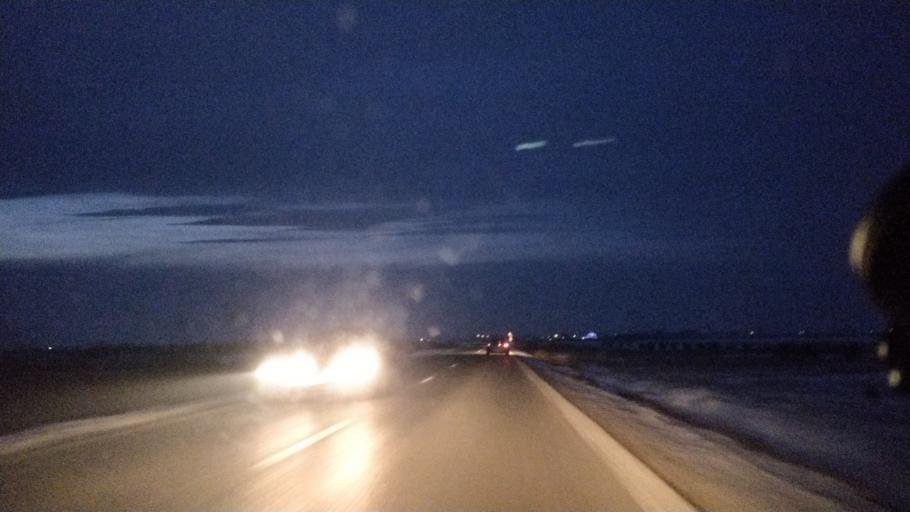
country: RO
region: Vrancea
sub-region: Comuna Milcovul
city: Milcovul
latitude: 45.6731
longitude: 27.2563
